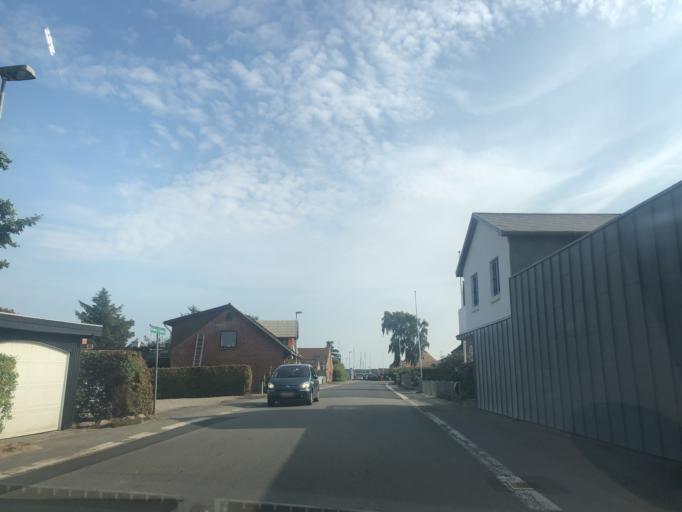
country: DK
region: North Denmark
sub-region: Morso Kommune
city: Nykobing Mors
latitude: 56.8061
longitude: 9.0202
